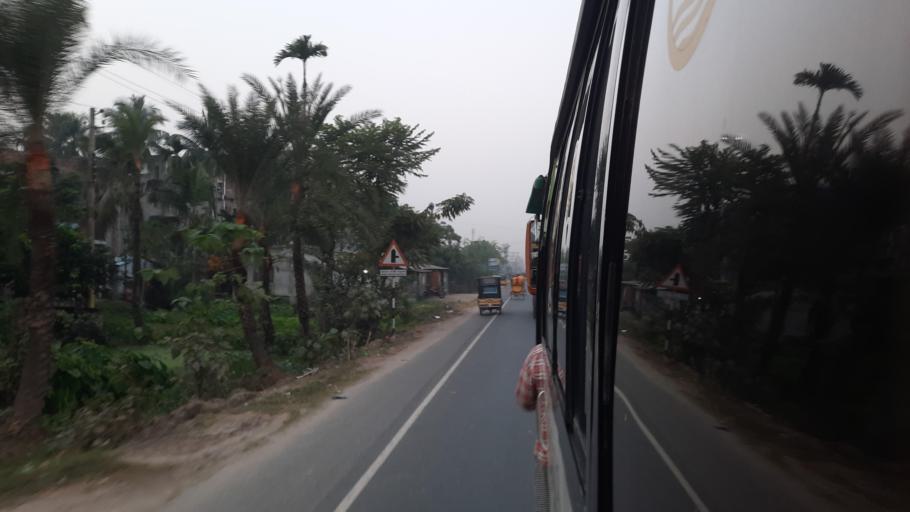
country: BD
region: Khulna
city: Jessore
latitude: 23.1666
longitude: 89.1933
